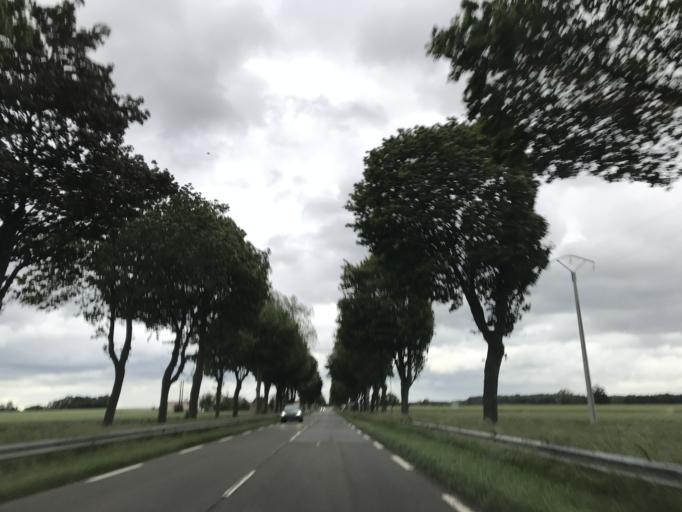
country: FR
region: Ile-de-France
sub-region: Departement des Yvelines
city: Bennecourt
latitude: 49.0238
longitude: 1.5140
